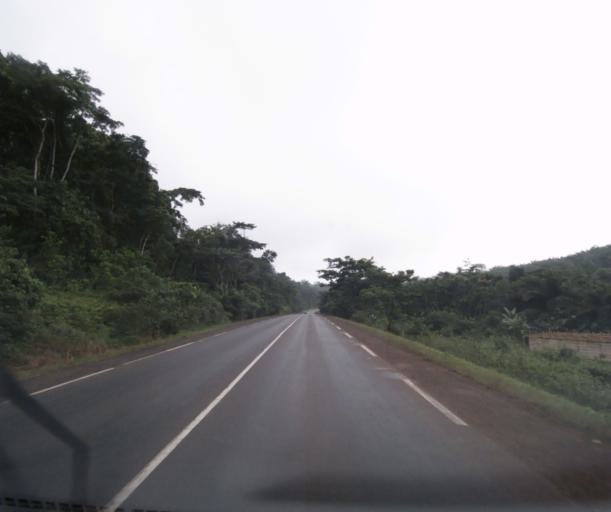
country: CM
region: Centre
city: Mbankomo
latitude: 3.7649
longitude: 11.1967
